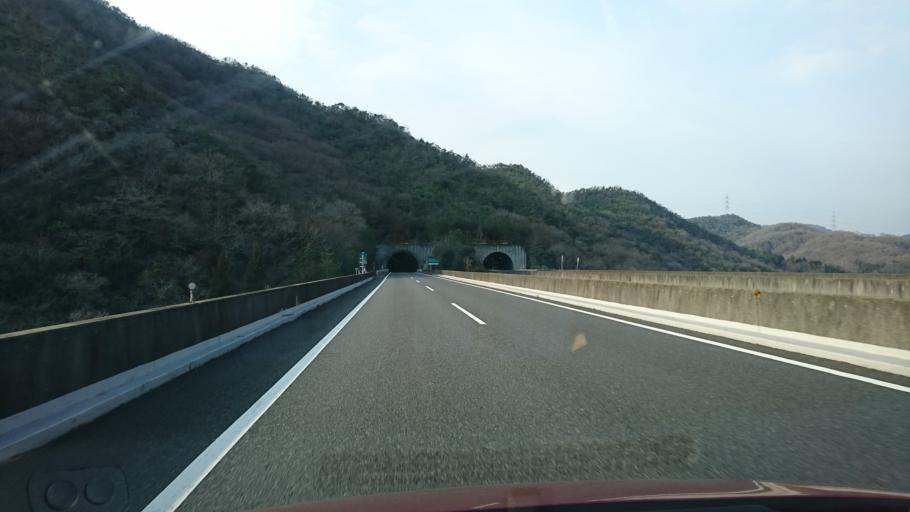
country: JP
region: Okayama
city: Okayama-shi
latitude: 34.7847
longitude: 134.1371
